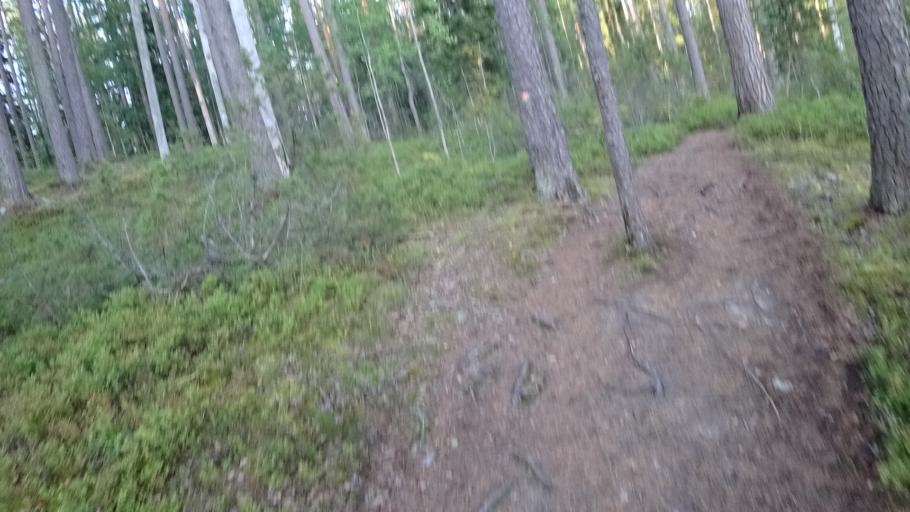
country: FI
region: North Karelia
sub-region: Joensuu
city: Ilomantsi
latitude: 62.5813
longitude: 31.1705
